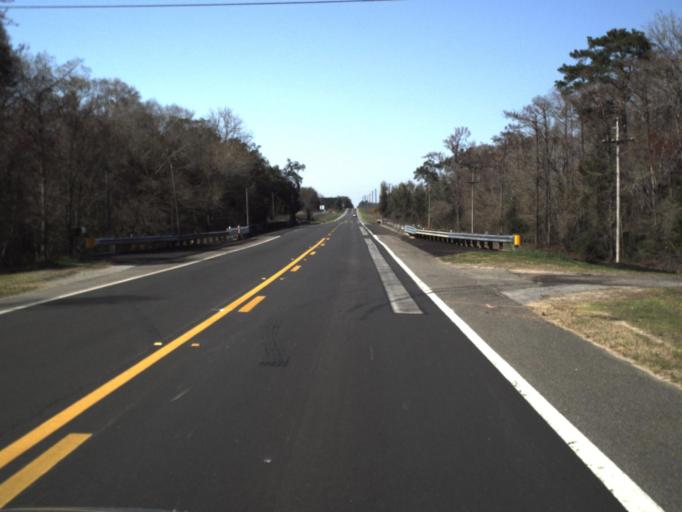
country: US
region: Florida
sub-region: Jackson County
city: Marianna
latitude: 30.6564
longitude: -85.1619
